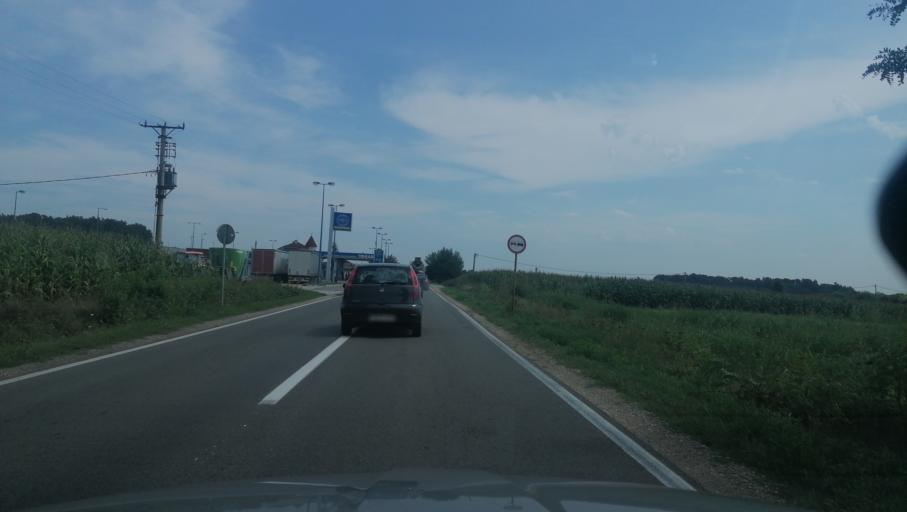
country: HR
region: Vukovarsko-Srijemska
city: Soljani
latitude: 44.8336
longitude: 18.9852
